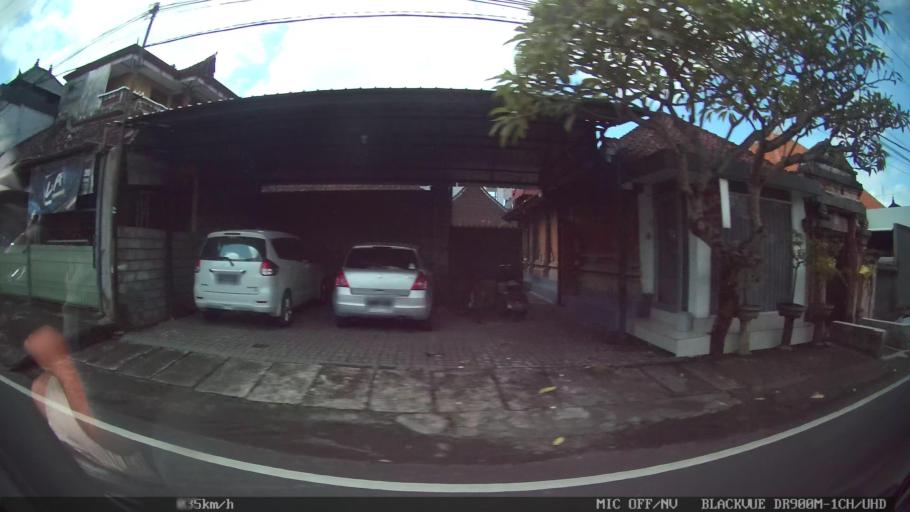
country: ID
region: Bali
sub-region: Kabupaten Gianyar
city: Ubud
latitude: -8.5551
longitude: 115.2869
